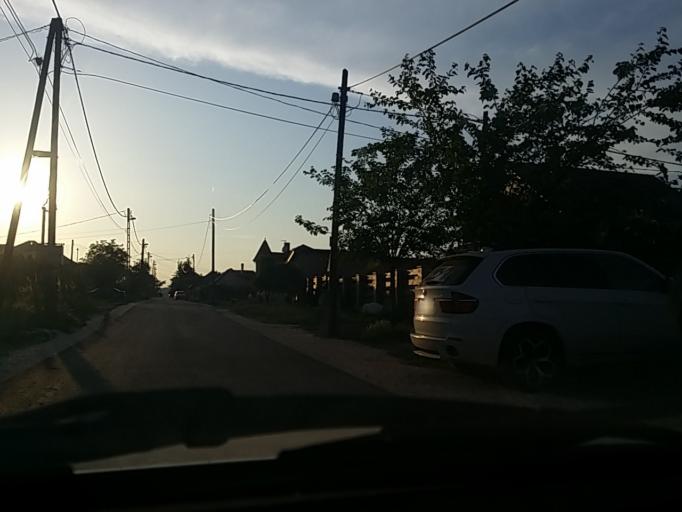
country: HU
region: Pest
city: Urom
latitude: 47.5833
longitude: 19.0137
